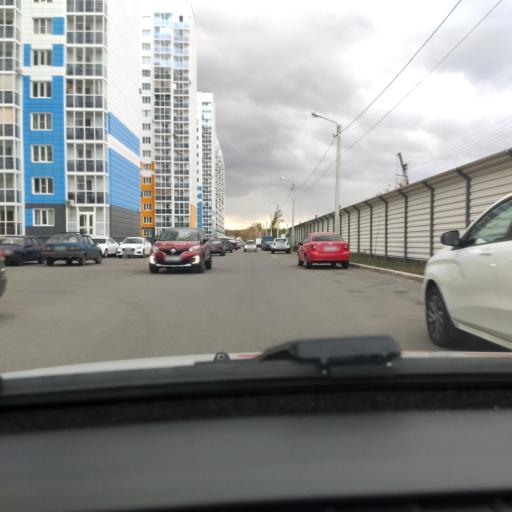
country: RU
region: Voronezj
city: Podgornoye
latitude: 51.7604
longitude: 39.1848
